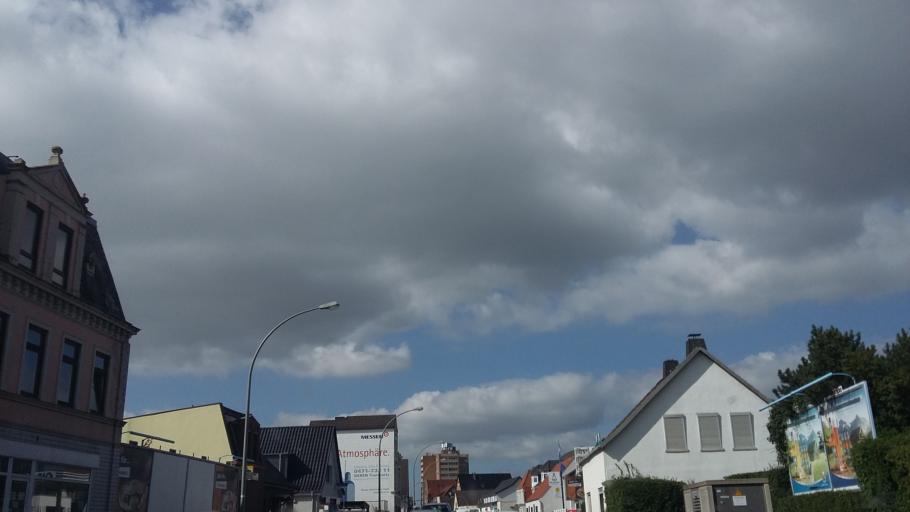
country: DE
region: Bremen
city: Bremerhaven
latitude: 53.5019
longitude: 8.6003
